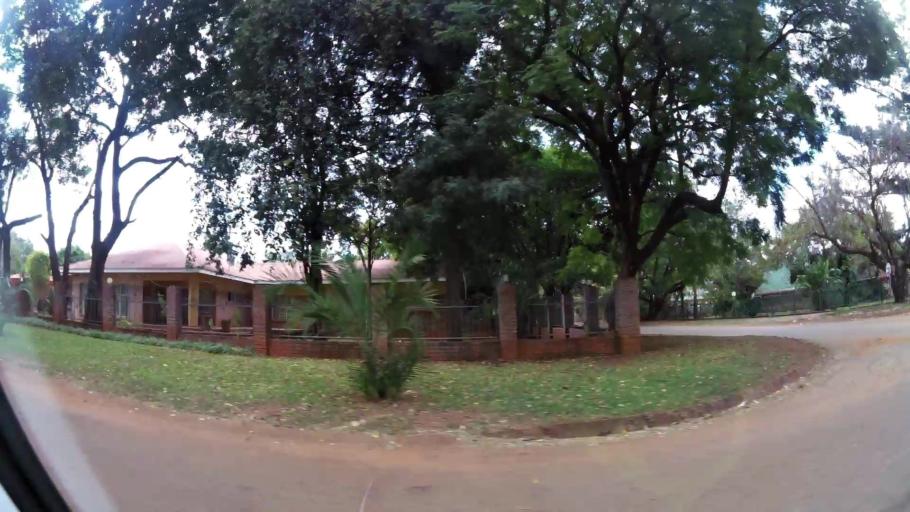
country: ZA
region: Limpopo
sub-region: Waterberg District Municipality
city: Modimolle
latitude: -24.5105
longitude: 28.7192
